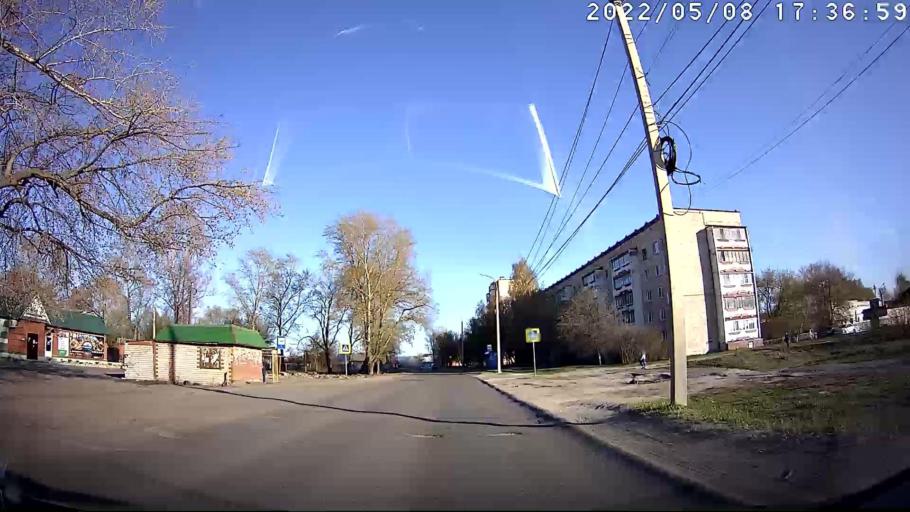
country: RU
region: Mariy-El
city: Volzhsk
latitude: 55.8684
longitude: 48.3697
